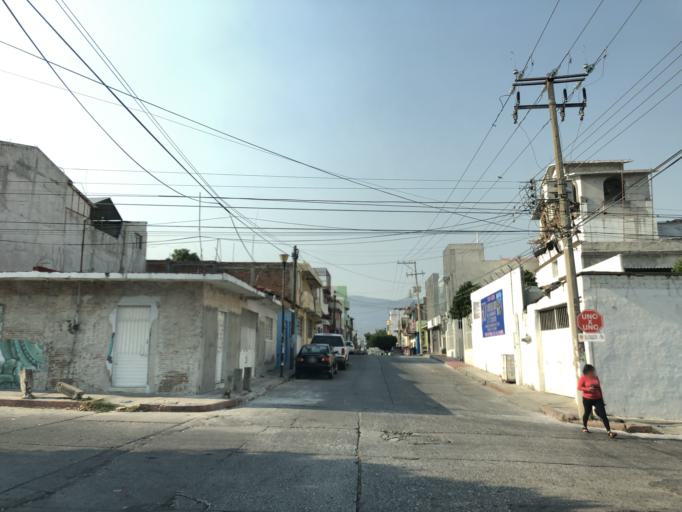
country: MX
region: Chiapas
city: Tuxtla Gutierrez
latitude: 16.7508
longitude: -93.1219
